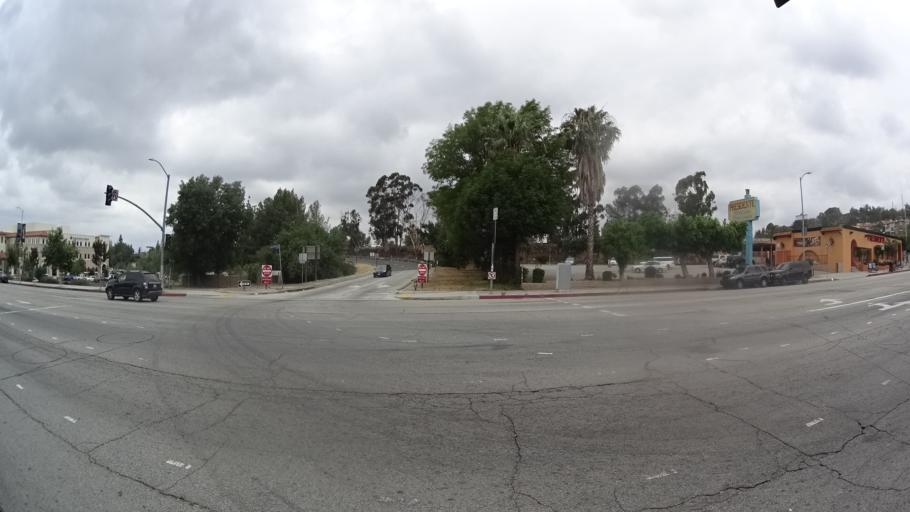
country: US
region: California
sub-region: Los Angeles County
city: San Fernando
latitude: 34.2784
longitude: -118.4686
